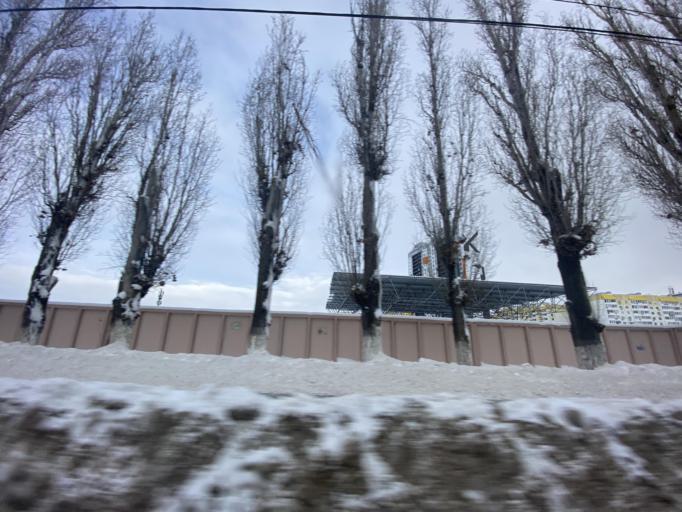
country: RU
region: Saratov
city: Engel's
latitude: 51.4995
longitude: 46.0862
